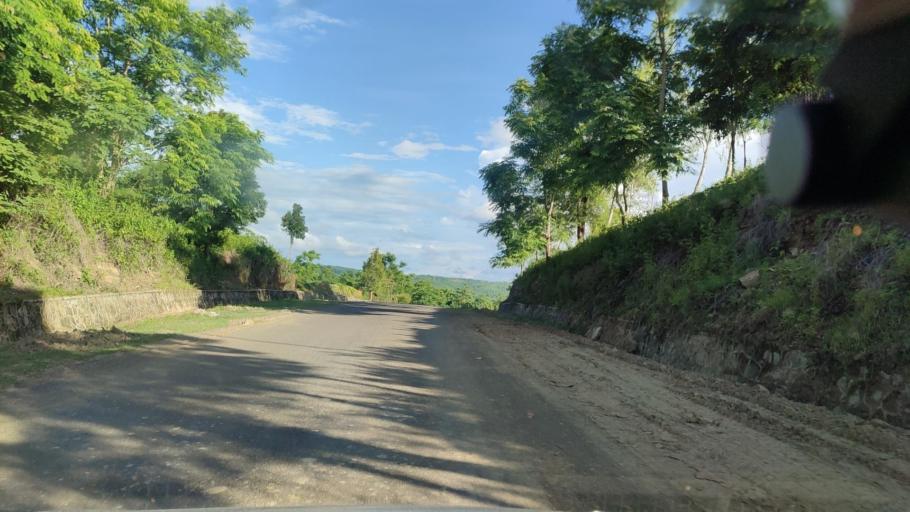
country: MM
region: Magway
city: Taungdwingyi
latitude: 20.0920
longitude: 95.7491
